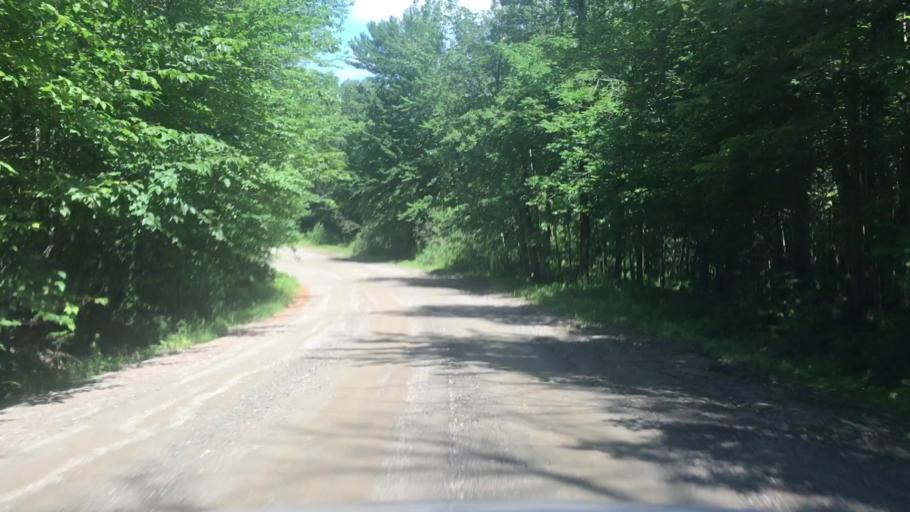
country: US
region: Maine
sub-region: Waldo County
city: Searsmont
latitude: 44.4703
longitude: -69.2973
